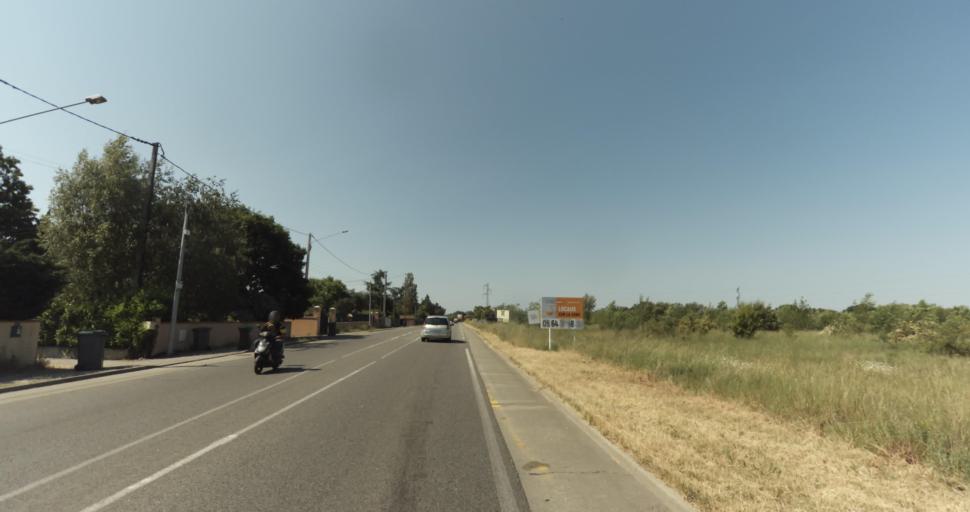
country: FR
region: Midi-Pyrenees
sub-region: Departement de la Haute-Garonne
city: La Salvetat-Saint-Gilles
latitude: 43.5857
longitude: 1.2799
